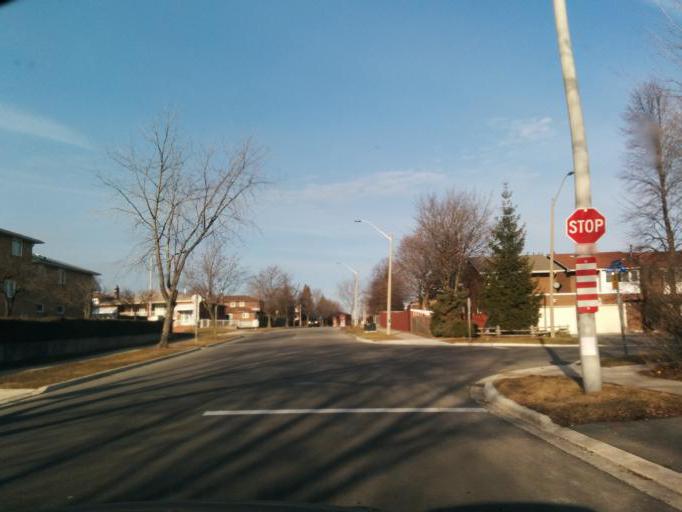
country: CA
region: Ontario
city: Mississauga
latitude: 43.5993
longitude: -79.5993
